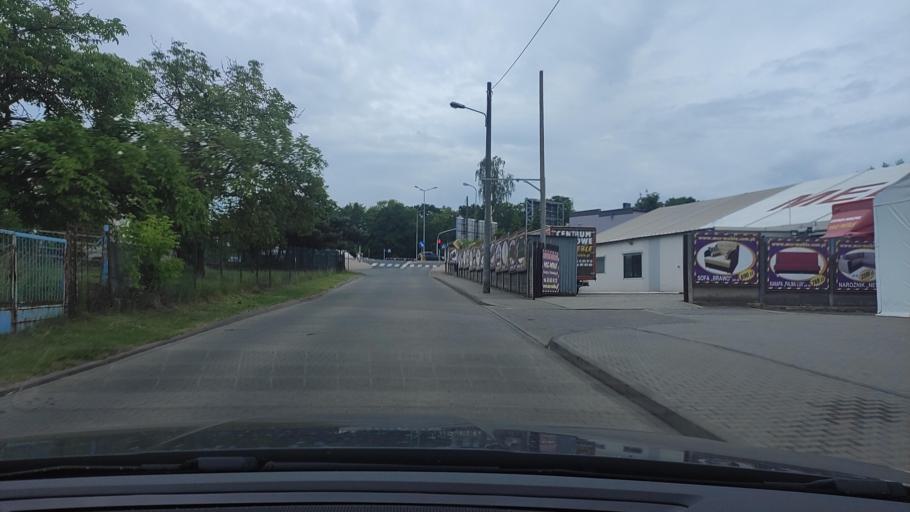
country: PL
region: Greater Poland Voivodeship
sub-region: Powiat poznanski
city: Swarzedz
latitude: 52.4061
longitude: 17.0613
